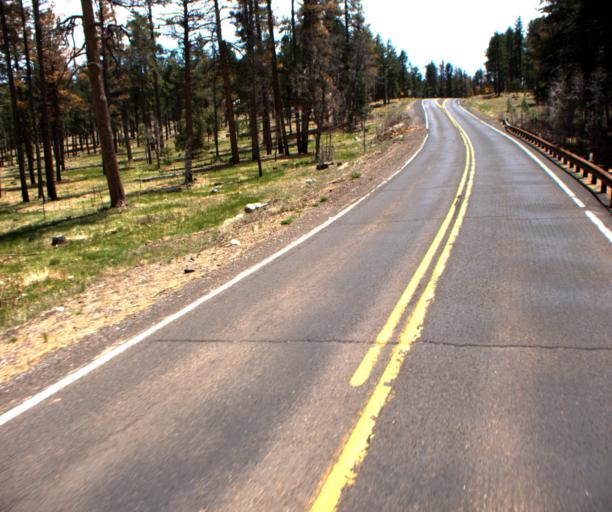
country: US
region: Arizona
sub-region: Coconino County
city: Kachina Village
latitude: 35.0405
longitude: -111.7338
